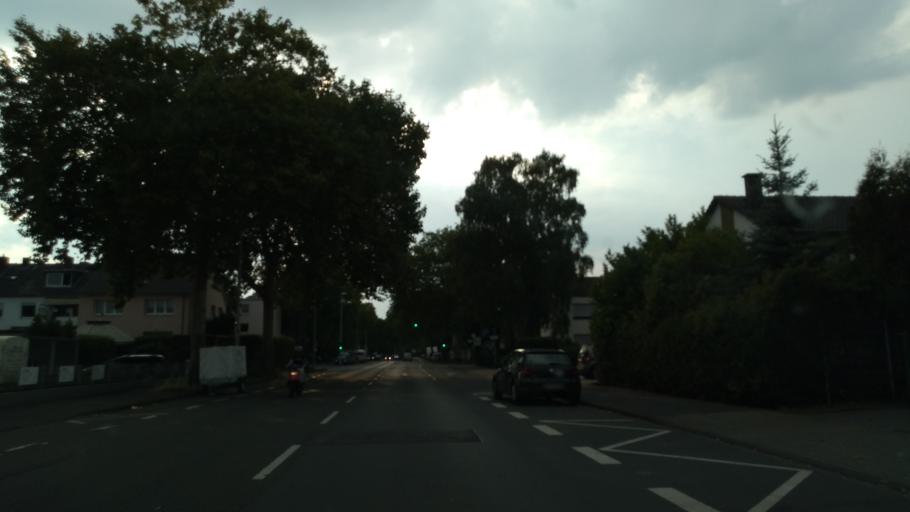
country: DE
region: North Rhine-Westphalia
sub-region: Regierungsbezirk Koln
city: Alfter
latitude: 50.7397
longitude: 7.0520
